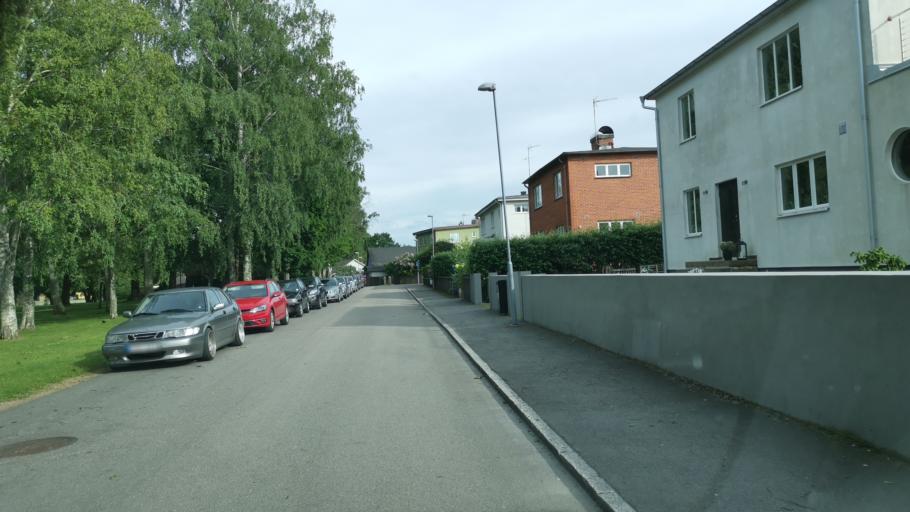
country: SE
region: Vaestra Goetaland
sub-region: Vanersborgs Kommun
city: Vanersborg
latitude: 58.3828
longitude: 12.3320
